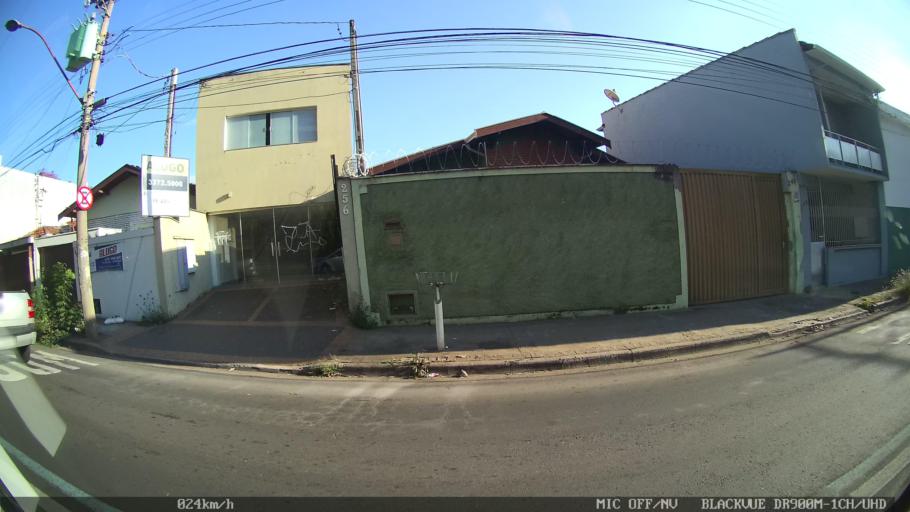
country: BR
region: Sao Paulo
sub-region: Piracicaba
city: Piracicaba
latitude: -22.7152
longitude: -47.6474
